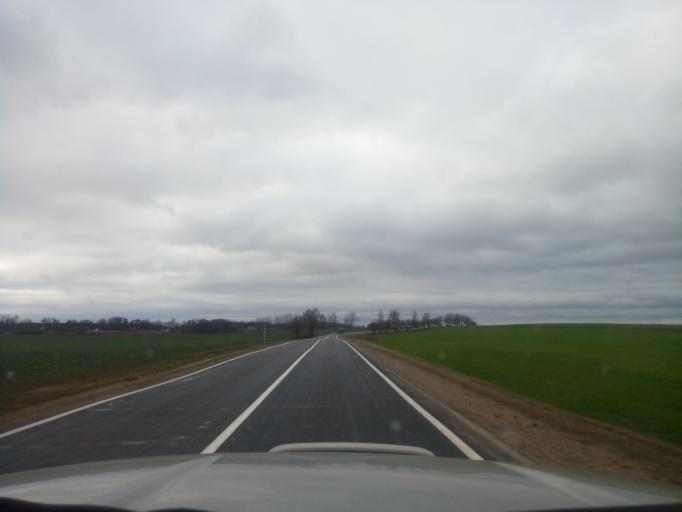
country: BY
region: Minsk
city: Kapyl'
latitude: 53.1869
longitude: 27.1820
